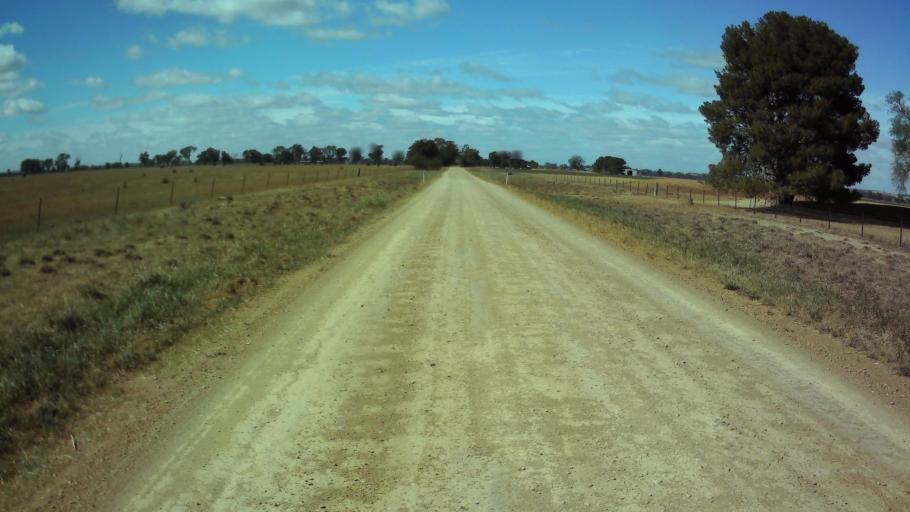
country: AU
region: New South Wales
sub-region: Weddin
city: Grenfell
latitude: -34.0223
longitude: 148.3187
